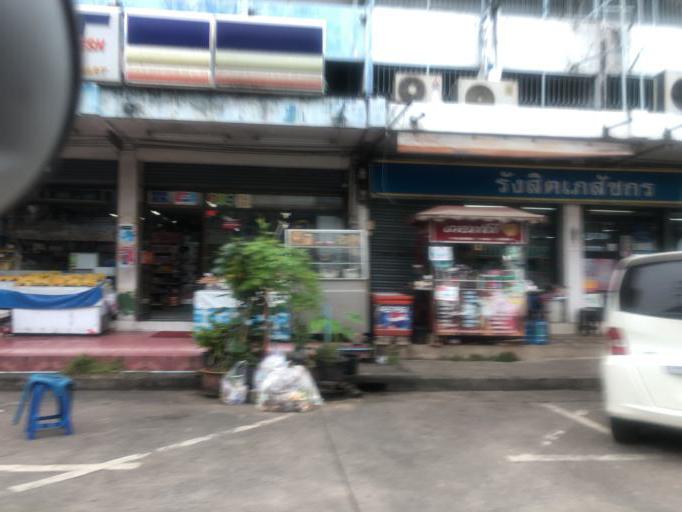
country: TH
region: Bangkok
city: Sai Mai
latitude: 13.9687
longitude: 100.6175
